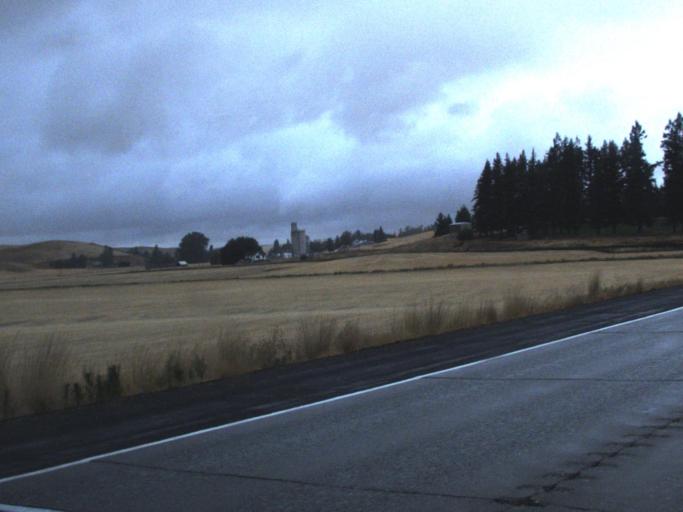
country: US
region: Washington
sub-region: Whitman County
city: Colfax
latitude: 47.1117
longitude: -117.3791
